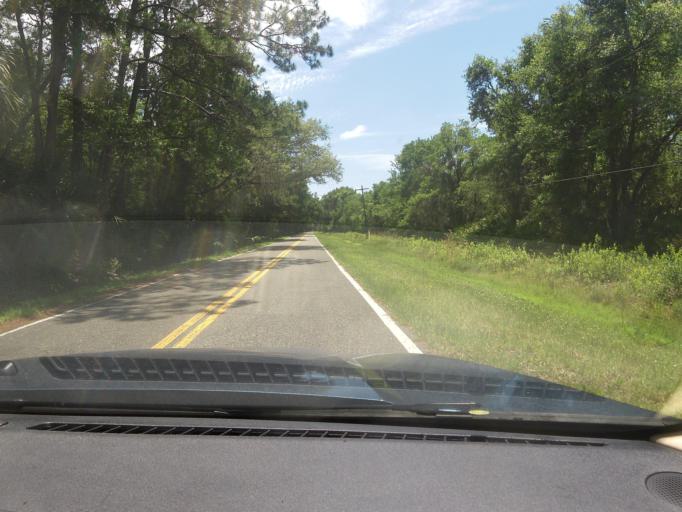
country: US
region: Florida
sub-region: Duval County
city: Atlantic Beach
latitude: 30.4507
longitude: -81.4651
